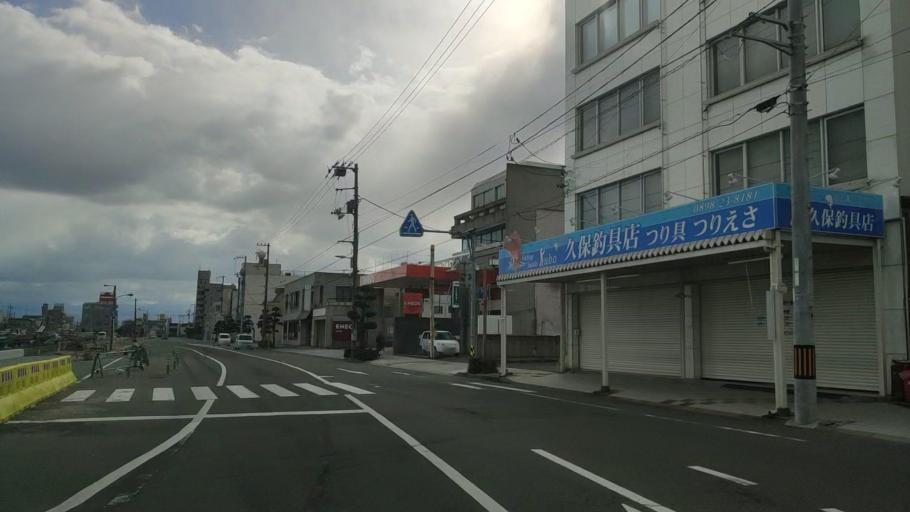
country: JP
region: Ehime
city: Saijo
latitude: 34.0685
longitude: 133.0047
